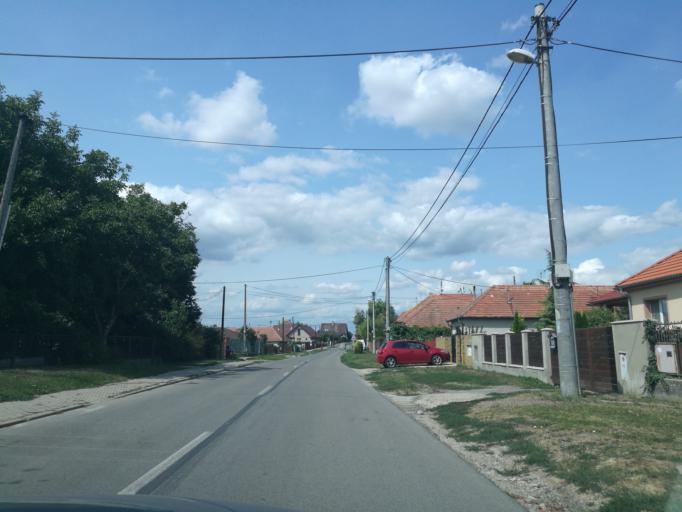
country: SK
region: Nitriansky
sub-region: Okres Nitra
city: Nitra
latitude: 48.2873
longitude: 18.1376
